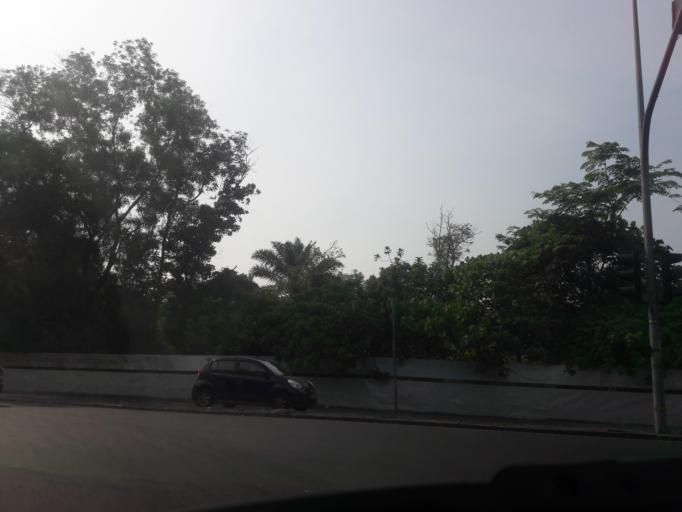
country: MY
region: Kedah
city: Kulim
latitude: 5.3460
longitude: 100.5198
